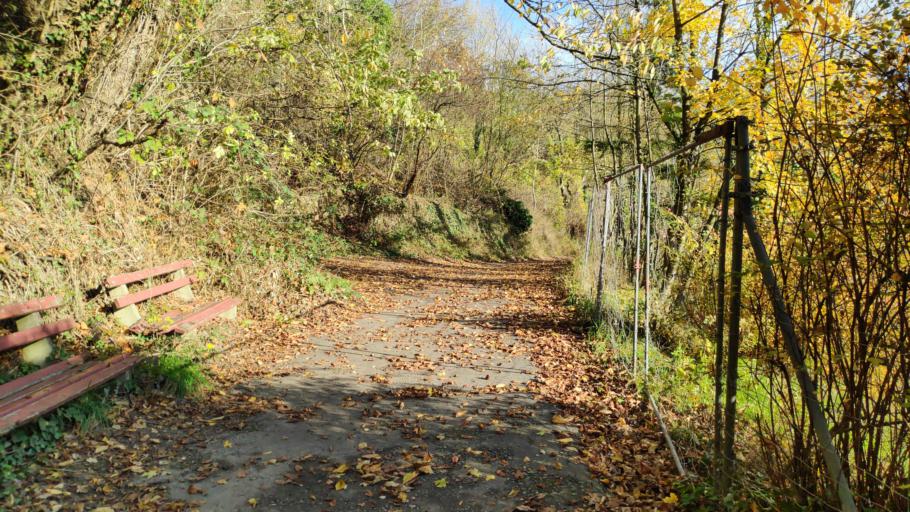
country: DE
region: Hesse
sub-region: Regierungsbezirk Darmstadt
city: Heppenheim an der Bergstrasse
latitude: 49.6469
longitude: 8.6548
